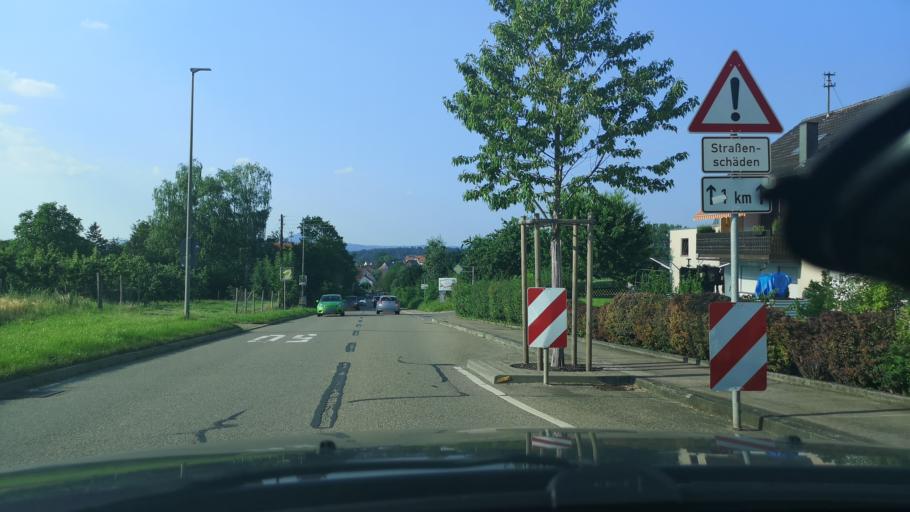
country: DE
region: Baden-Wuerttemberg
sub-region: Regierungsbezirk Stuttgart
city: Schlat
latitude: 48.6468
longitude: 9.7036
